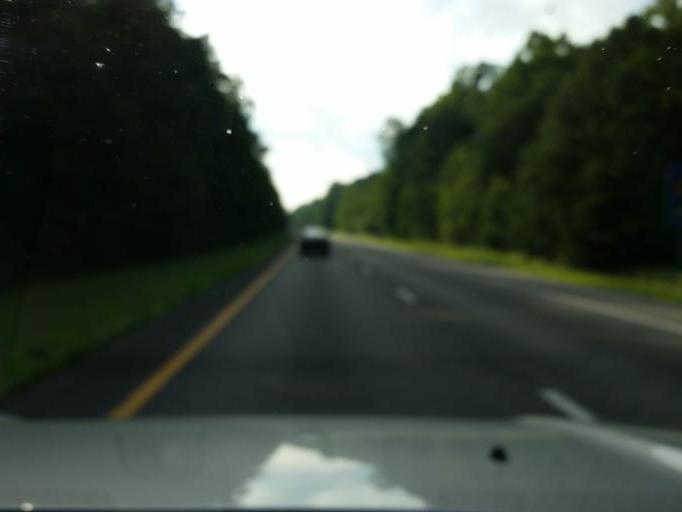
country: US
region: Virginia
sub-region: King William County
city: West Point
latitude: 37.4119
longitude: -76.7961
